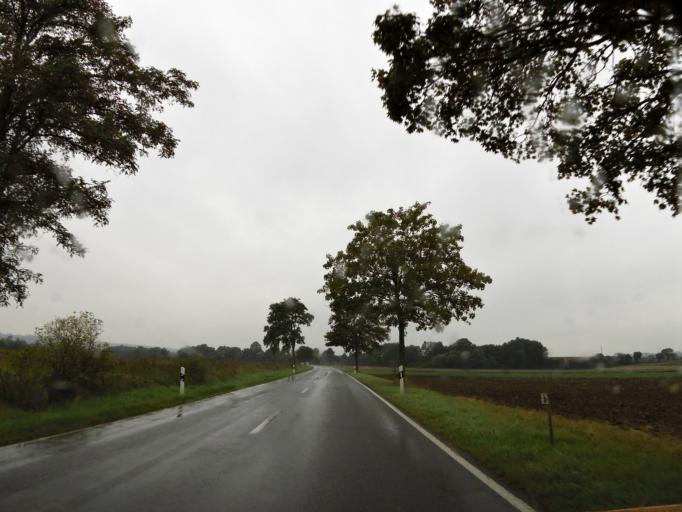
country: DE
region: Lower Saxony
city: Herzberg am Harz
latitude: 51.6310
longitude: 10.3443
